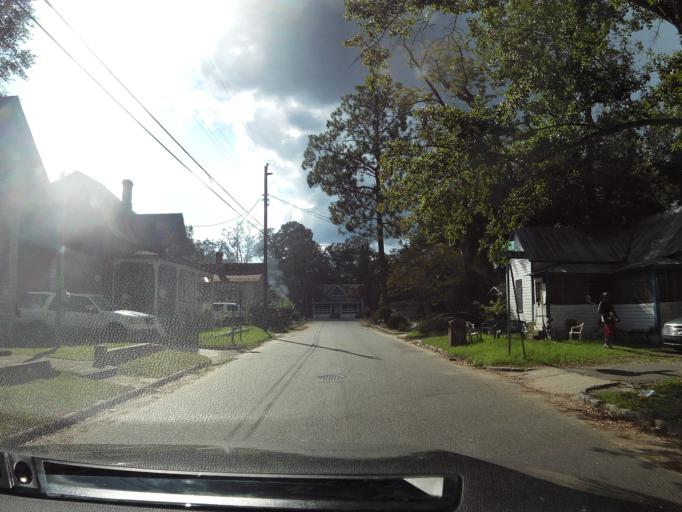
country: US
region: Georgia
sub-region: Lowndes County
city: Valdosta
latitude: 30.8318
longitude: -83.2899
